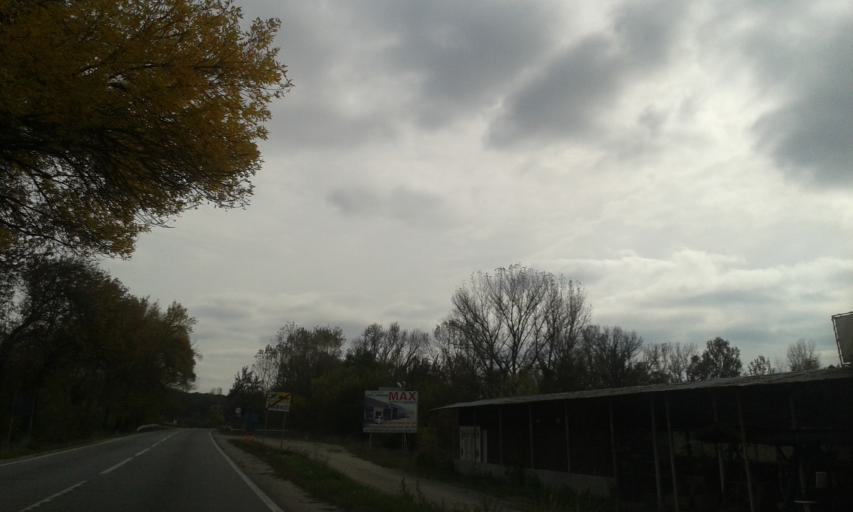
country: RO
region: Gorj
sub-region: Comuna Balanesti
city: Balanesti
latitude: 45.0383
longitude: 23.3698
